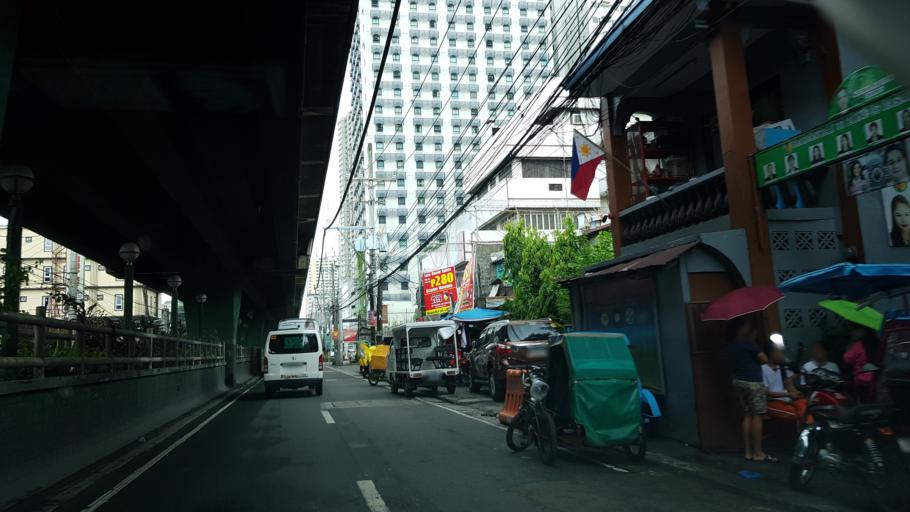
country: PH
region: Metro Manila
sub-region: City of Manila
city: Port Area
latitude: 14.5598
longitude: 120.9961
